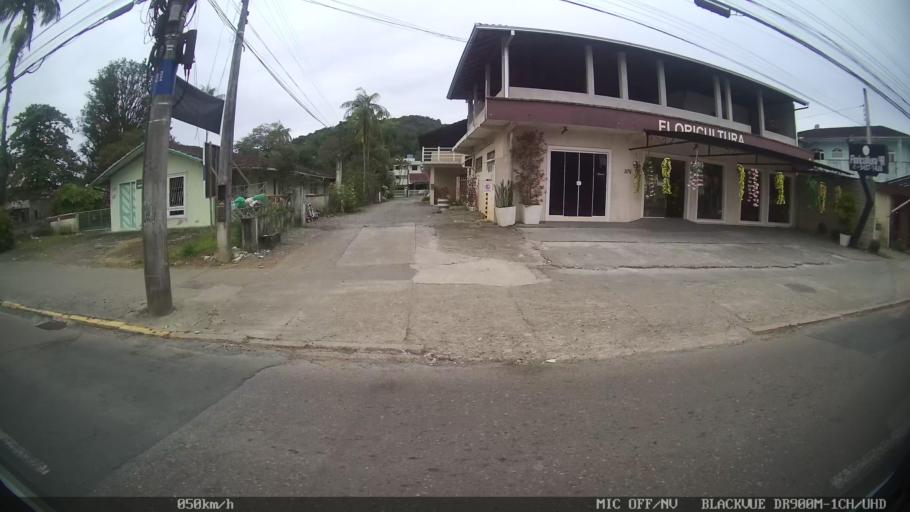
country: BR
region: Santa Catarina
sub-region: Joinville
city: Joinville
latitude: -26.2776
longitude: -48.8351
